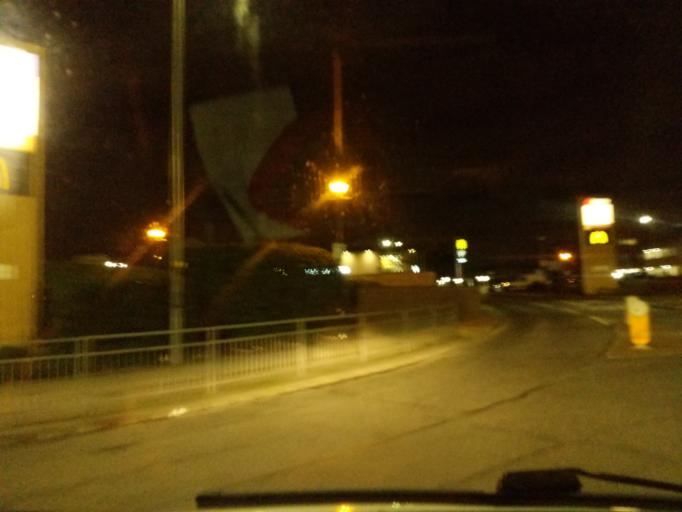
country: GB
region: England
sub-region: St. Helens
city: St Helens
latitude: 53.4511
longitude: -2.7393
